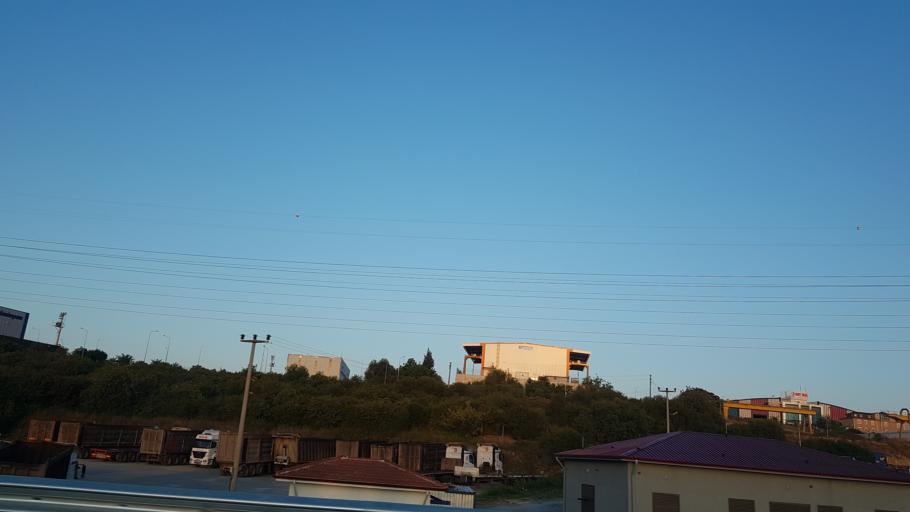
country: TR
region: Kocaeli
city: Tavsanli
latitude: 40.8078
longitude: 29.5195
